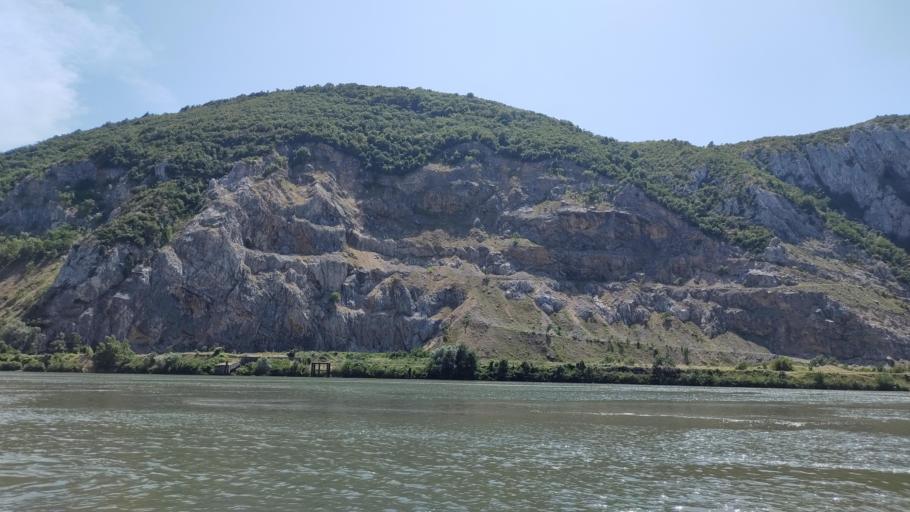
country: RO
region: Caras-Severin
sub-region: Comuna Pescari
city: Coronini
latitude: 44.6613
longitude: 21.7036
